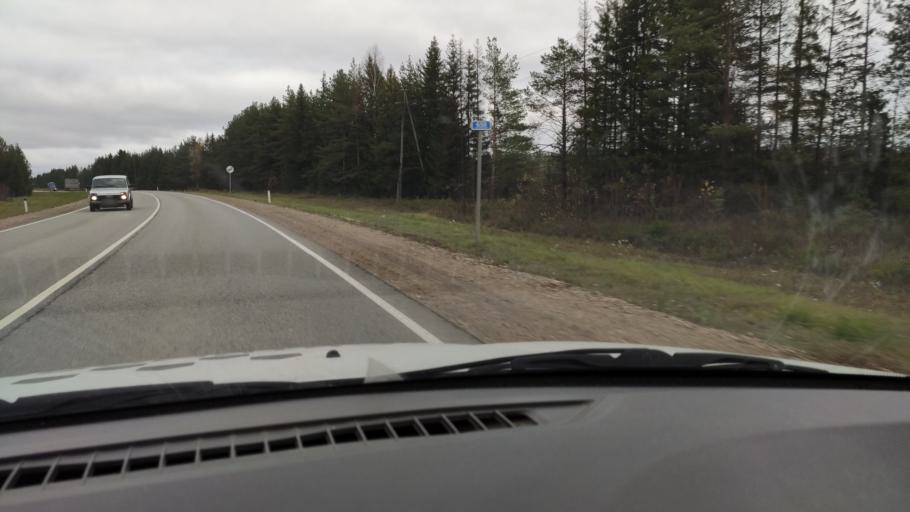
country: RU
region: Kirov
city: Slobodskoy
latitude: 58.7336
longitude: 50.2859
